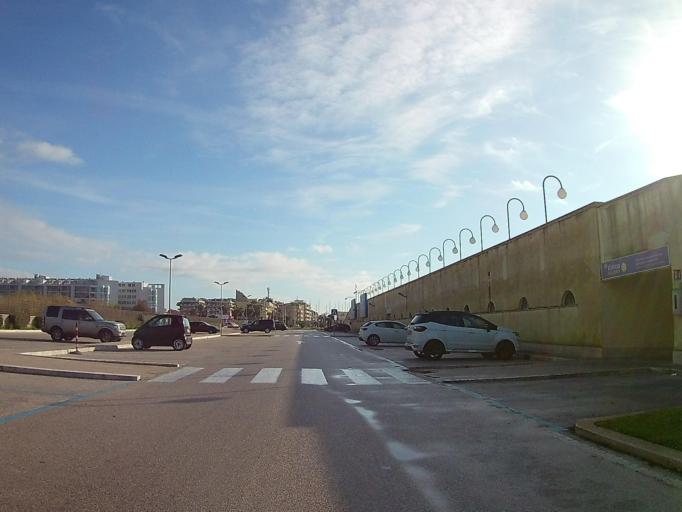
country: IT
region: Latium
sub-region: Citta metropolitana di Roma Capitale
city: Lido di Ostia
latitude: 41.7386
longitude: 12.2482
